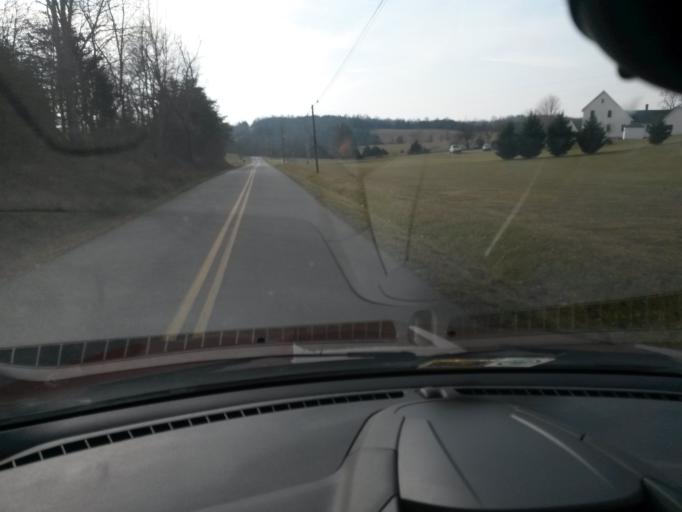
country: US
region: Virginia
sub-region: Botetourt County
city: Fincastle
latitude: 37.5676
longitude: -79.8829
